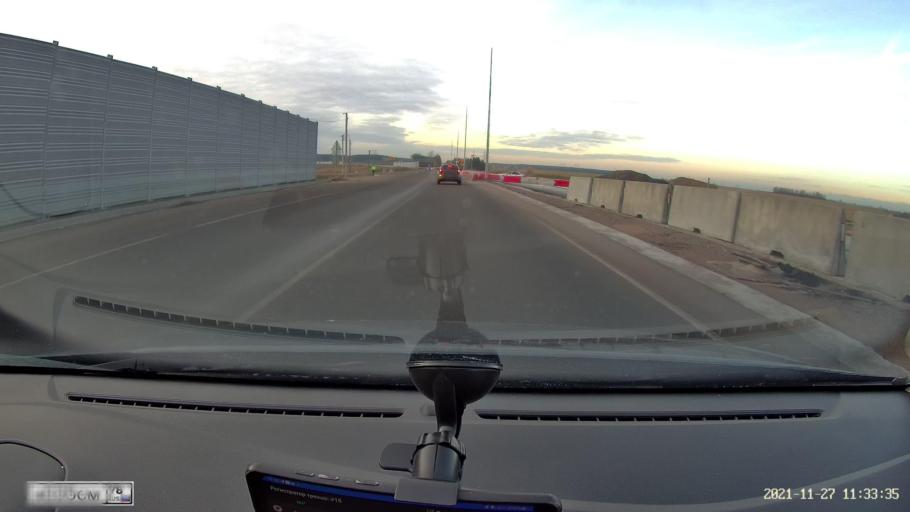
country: RU
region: Leningrad
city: Russko-Vysotskoye
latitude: 59.7094
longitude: 30.0140
